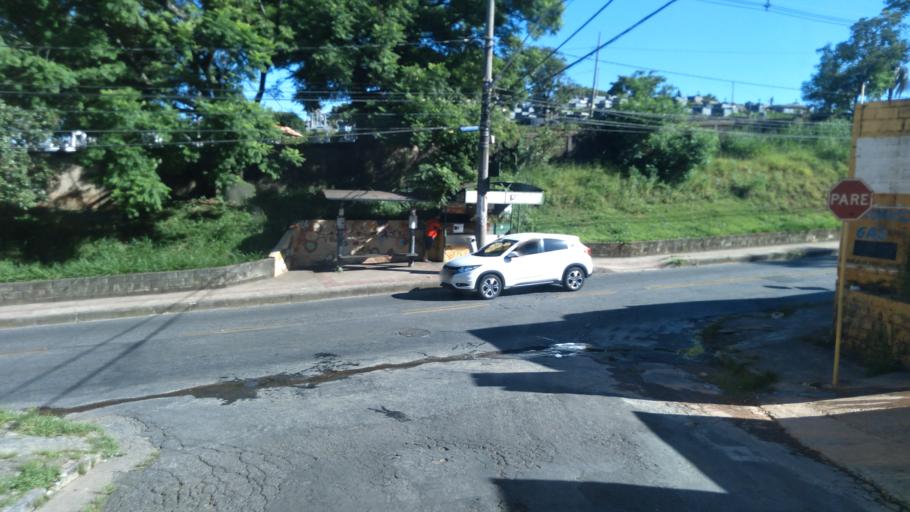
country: BR
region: Minas Gerais
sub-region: Belo Horizonte
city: Belo Horizonte
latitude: -19.9197
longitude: -43.8968
